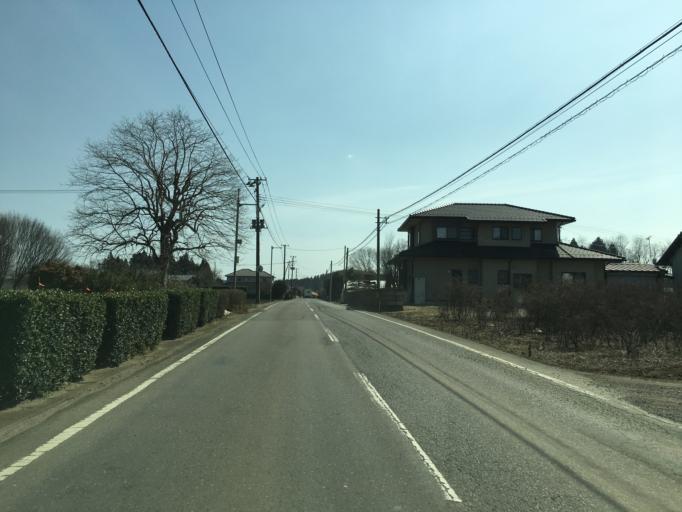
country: JP
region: Fukushima
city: Ishikawa
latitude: 37.1484
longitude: 140.3952
